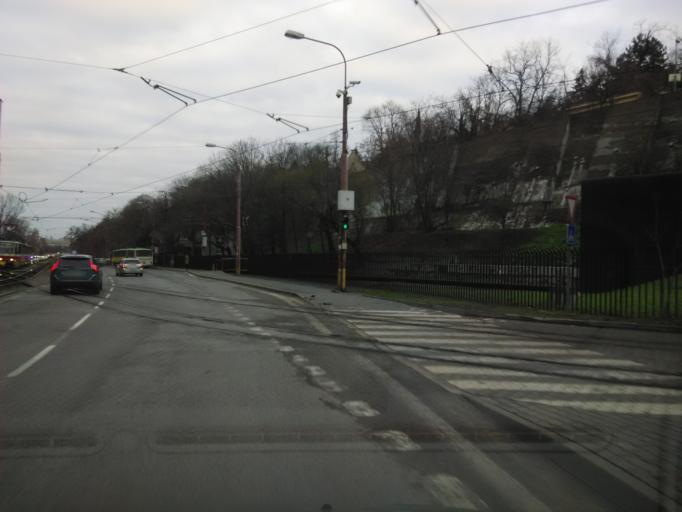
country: SK
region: Bratislavsky
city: Bratislava
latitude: 48.1416
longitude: 17.0918
